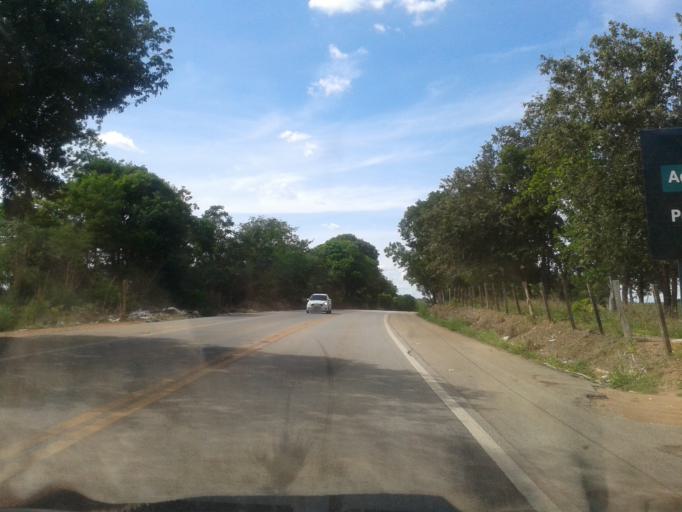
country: BR
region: Goias
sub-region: Itapuranga
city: Itapuranga
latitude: -15.4605
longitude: -50.3565
